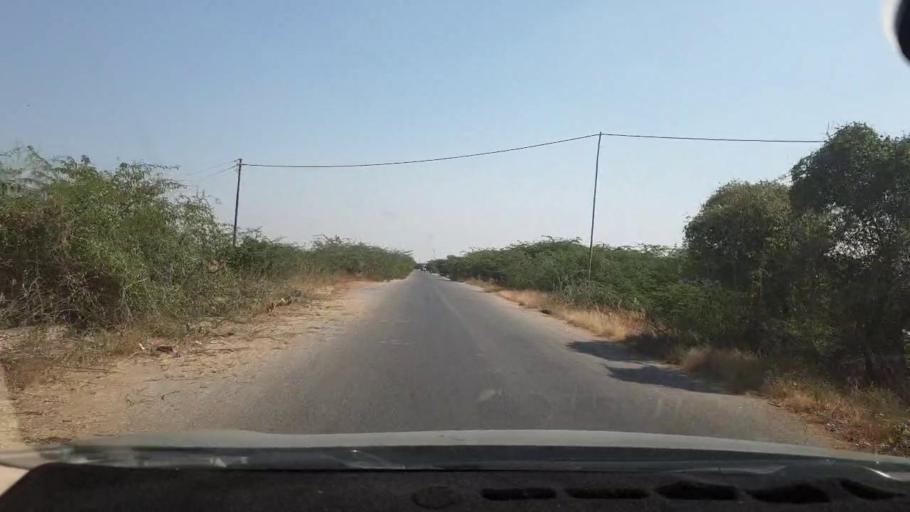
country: PK
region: Sindh
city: Malir Cantonment
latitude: 25.1412
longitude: 67.2007
